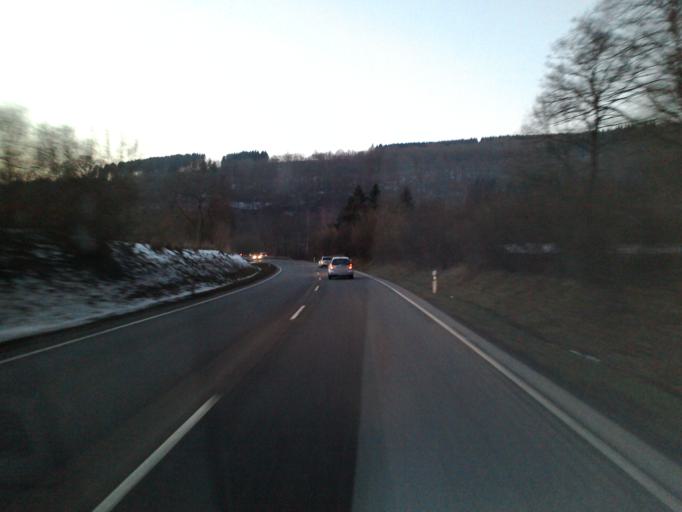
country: DE
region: North Rhine-Westphalia
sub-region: Regierungsbezirk Arnsberg
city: Olsberg
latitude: 51.3640
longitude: 8.4525
